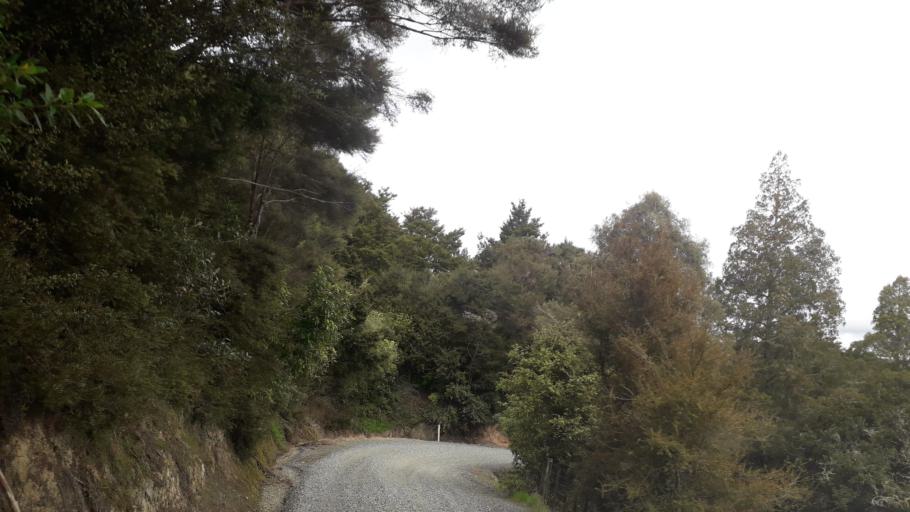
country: NZ
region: Northland
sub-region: Far North District
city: Waimate North
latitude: -35.1424
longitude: 173.7141
